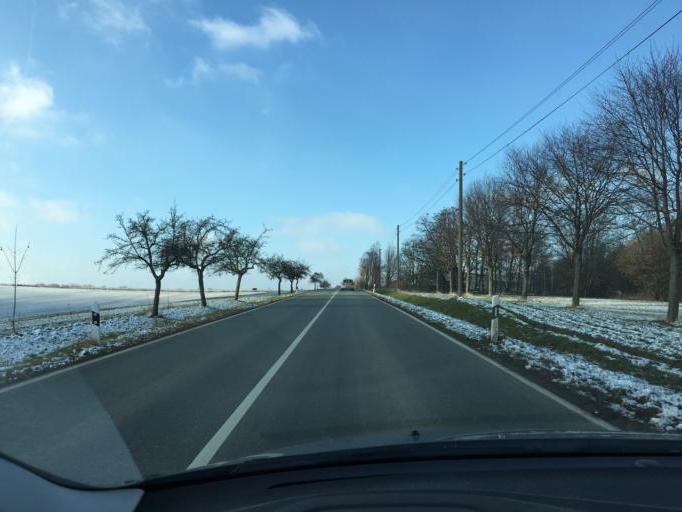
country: DE
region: Saxony
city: Penig
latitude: 50.9395
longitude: 12.6944
